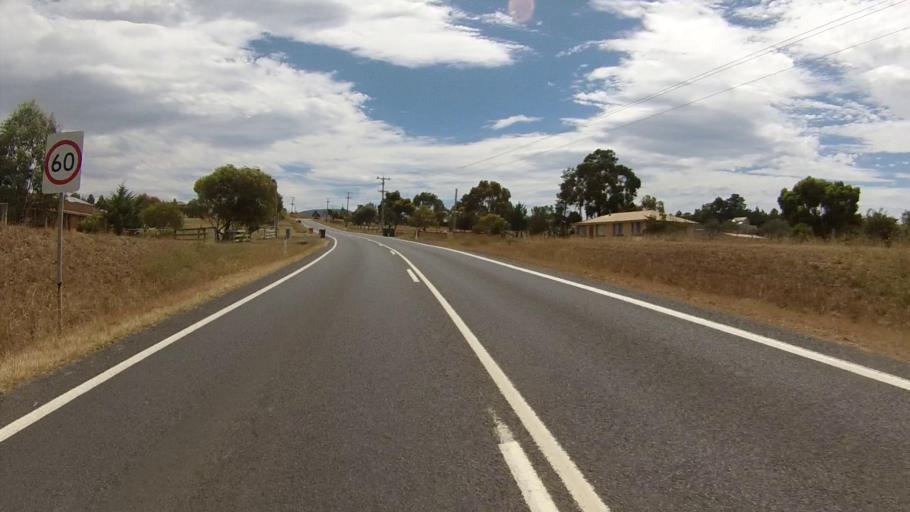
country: AU
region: Tasmania
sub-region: Brighton
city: Bridgewater
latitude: -42.7001
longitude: 147.2687
